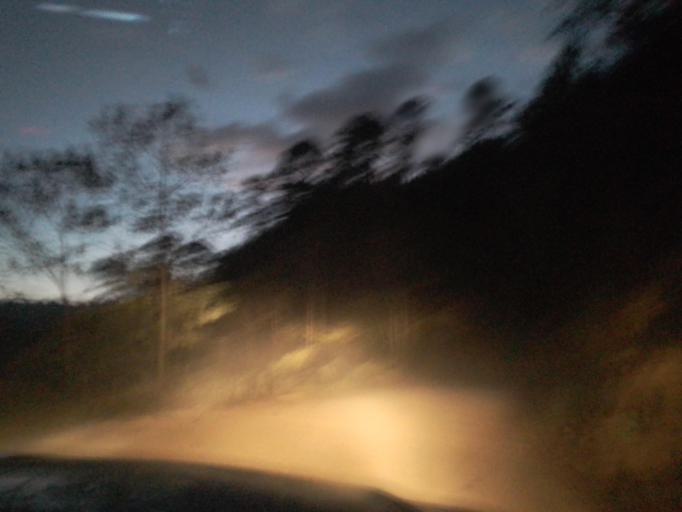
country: GT
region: San Marcos
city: Tacana
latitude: 15.2377
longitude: -92.1962
